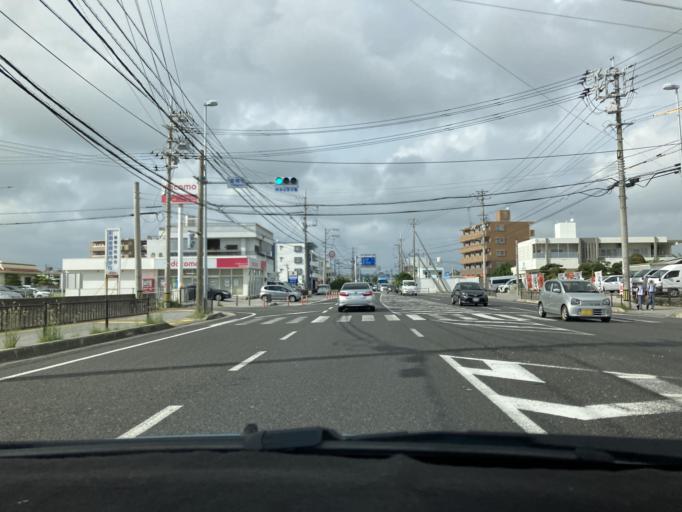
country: JP
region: Okinawa
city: Tomigusuku
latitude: 26.1631
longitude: 127.6690
